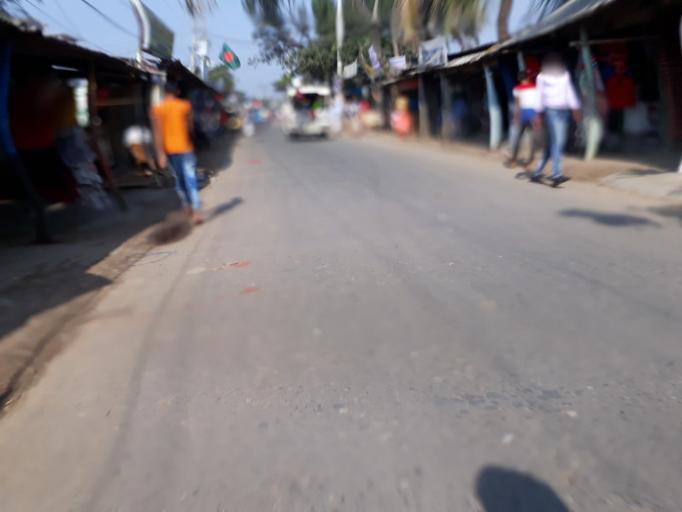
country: BD
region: Dhaka
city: Tungi
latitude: 23.8788
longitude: 90.3102
